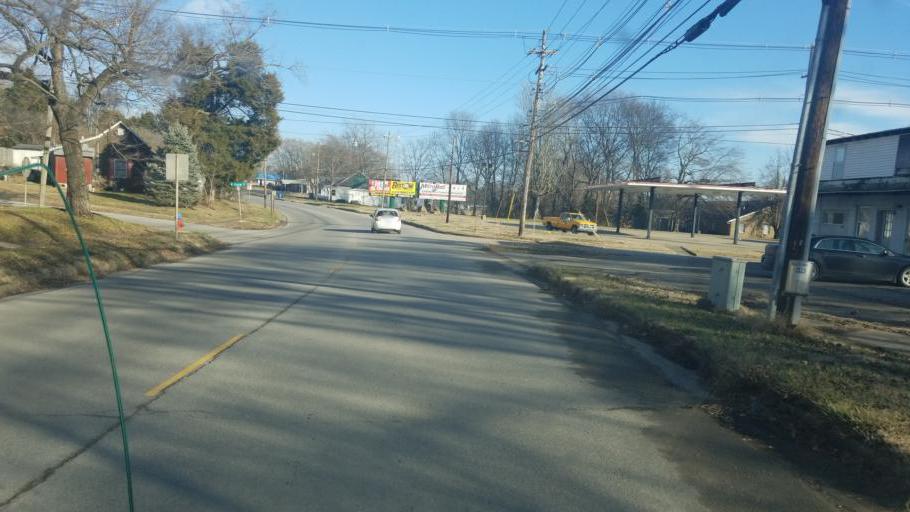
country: US
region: Illinois
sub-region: Wabash County
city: Mount Carmel
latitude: 38.4034
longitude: -87.7746
